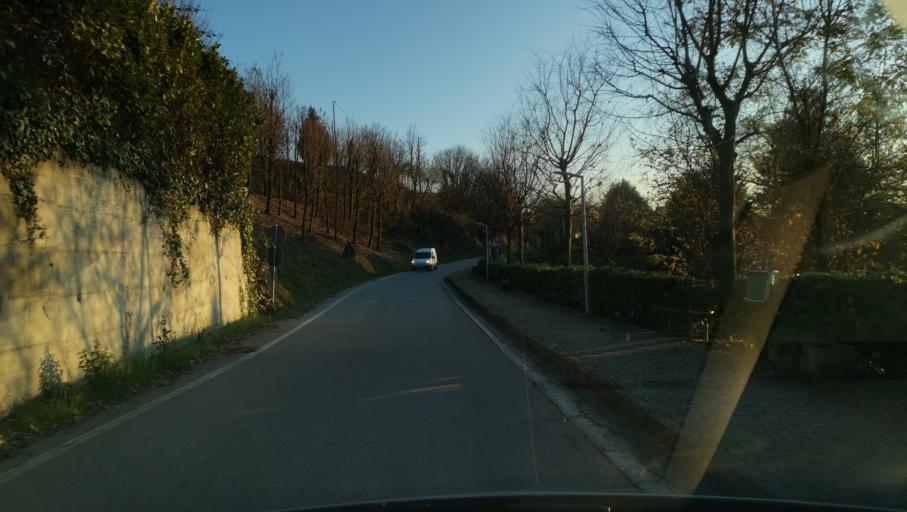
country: IT
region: Piedmont
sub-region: Provincia di Torino
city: Cinzano
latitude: 45.0920
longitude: 7.9236
